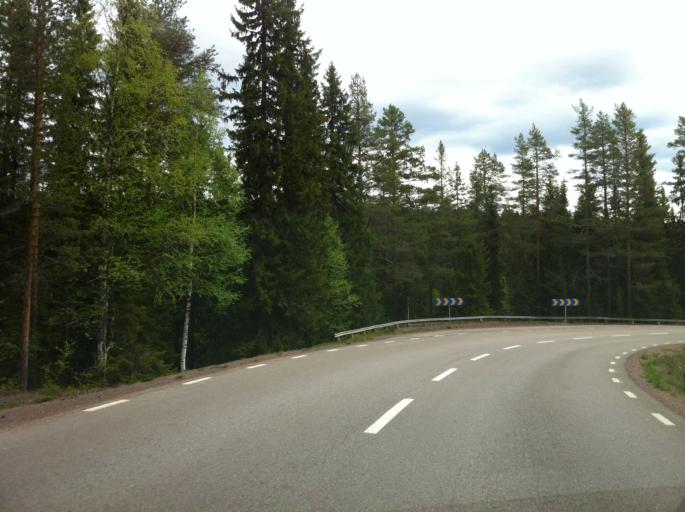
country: SE
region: Dalarna
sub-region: Malung-Saelens kommun
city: Malung
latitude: 61.2996
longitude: 13.1302
